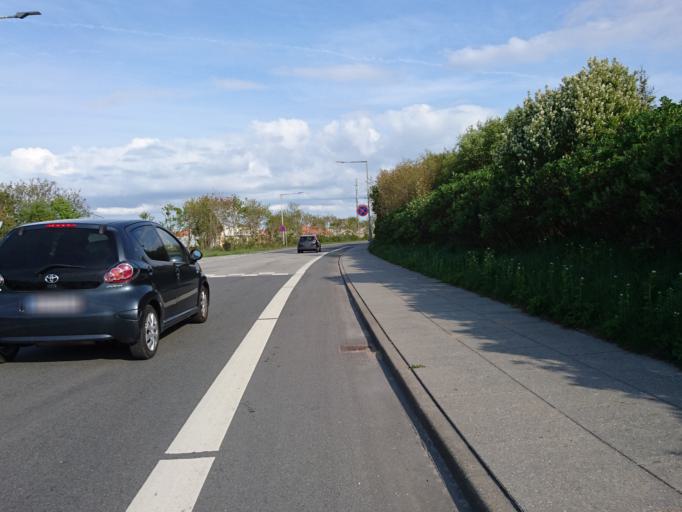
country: DK
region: North Denmark
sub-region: Frederikshavn Kommune
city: Skagen
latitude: 57.7290
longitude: 10.5572
